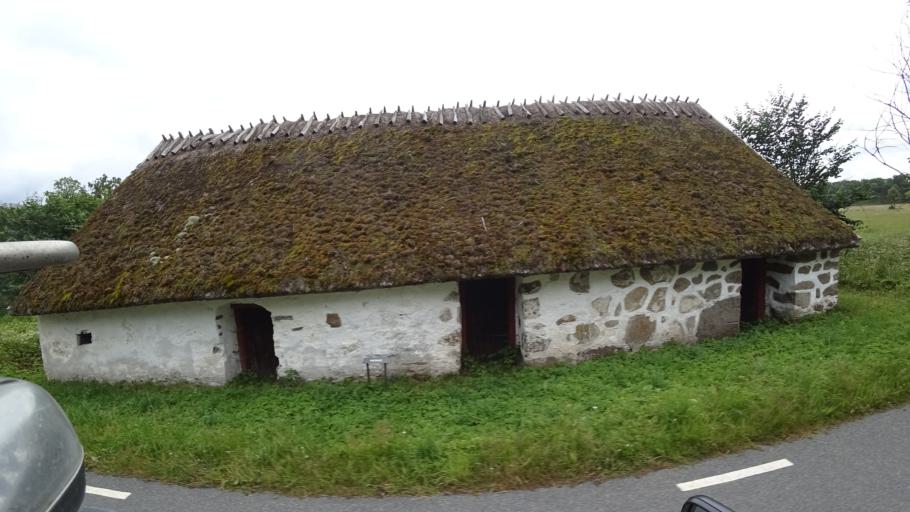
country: SE
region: Skane
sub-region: Kristianstads Kommun
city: Degeberga
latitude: 55.7136
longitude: 13.9844
